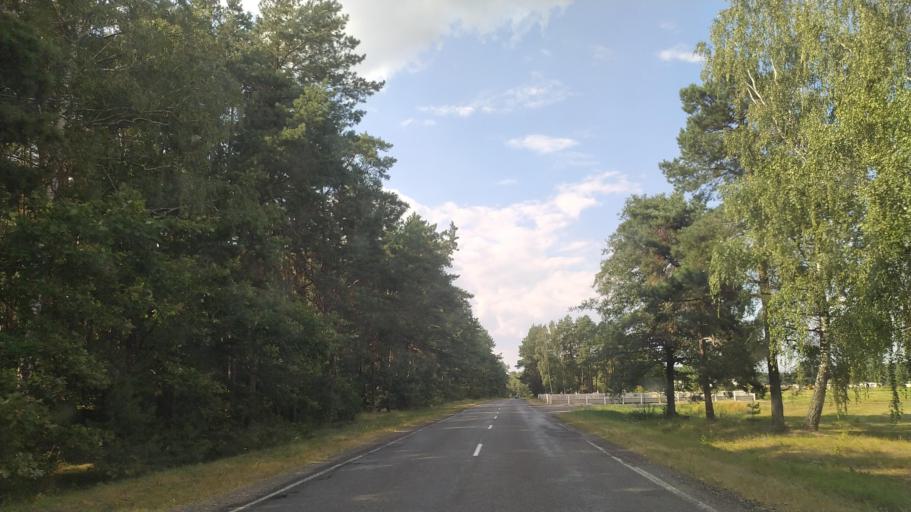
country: BY
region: Brest
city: Drahichyn
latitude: 52.3022
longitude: 25.0515
